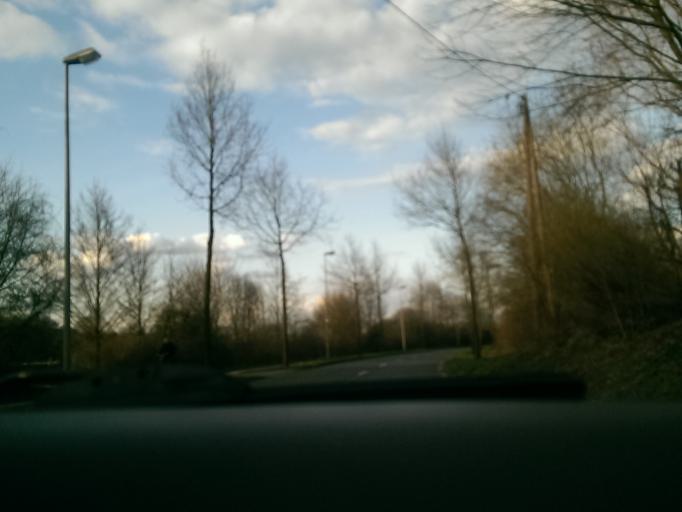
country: DE
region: North Rhine-Westphalia
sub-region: Regierungsbezirk Munster
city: Muenster
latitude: 51.9116
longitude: 7.6277
